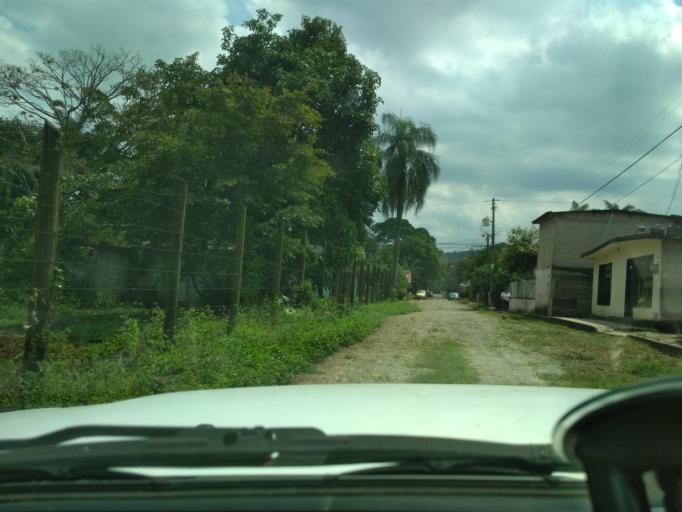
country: MX
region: Veracruz
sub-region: Fortin
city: Monte Salas
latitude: 18.9388
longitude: -97.0157
